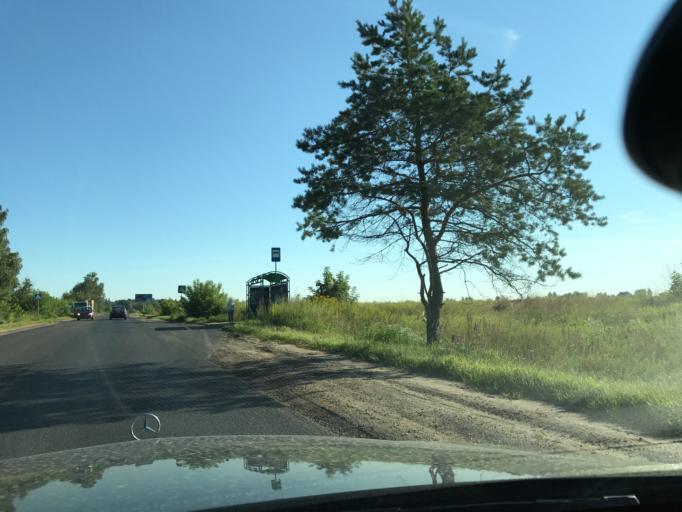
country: RU
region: Moskovskaya
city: Sverdlovskiy
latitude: 55.8816
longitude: 38.1608
